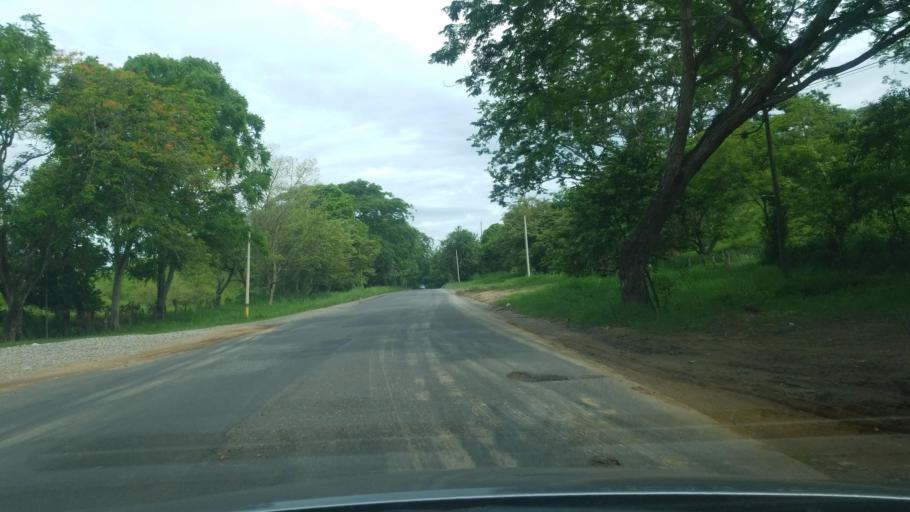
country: HN
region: Santa Barbara
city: Camalote
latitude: 15.3318
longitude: -88.3431
